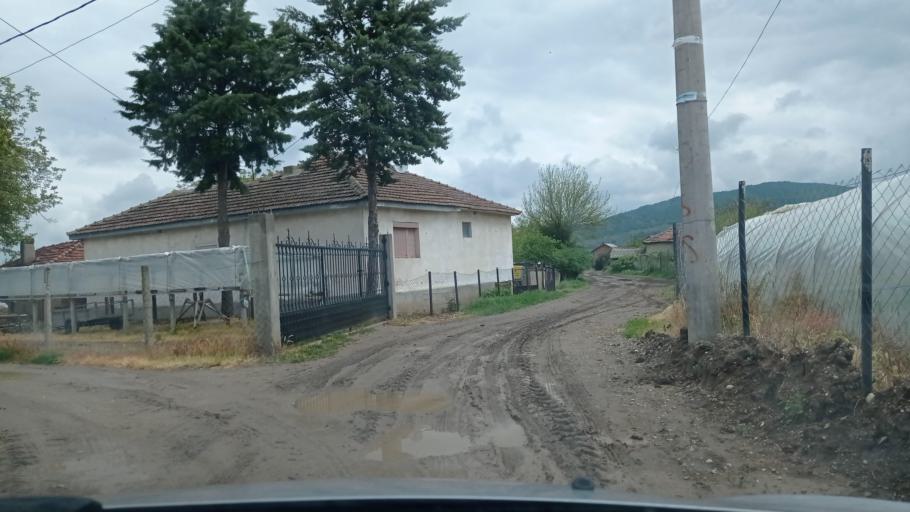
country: MK
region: Lozovo
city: Lozovo
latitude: 41.7658
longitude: 21.8953
